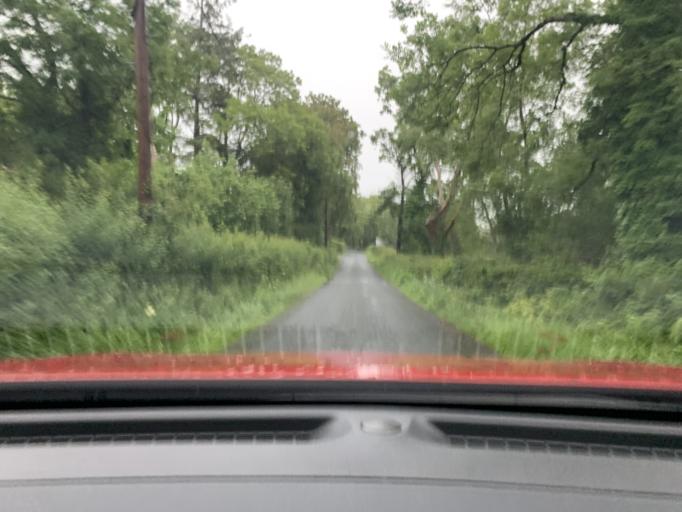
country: IE
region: Connaught
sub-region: Sligo
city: Sligo
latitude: 54.3194
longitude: -8.4689
